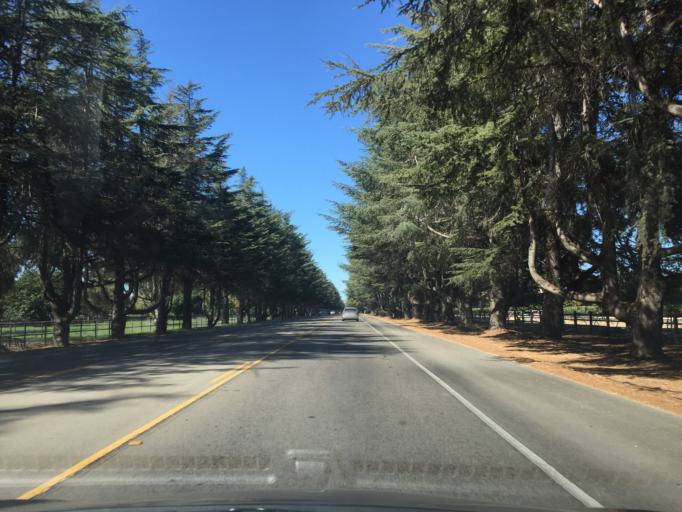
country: US
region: California
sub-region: Santa Barbara County
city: Solvang
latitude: 34.5999
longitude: -120.1613
